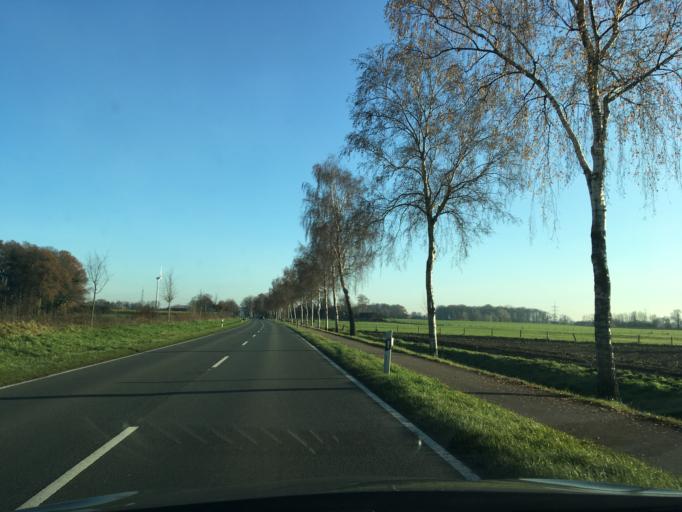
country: DE
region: North Rhine-Westphalia
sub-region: Regierungsbezirk Munster
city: Ahaus
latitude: 52.1109
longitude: 6.9519
